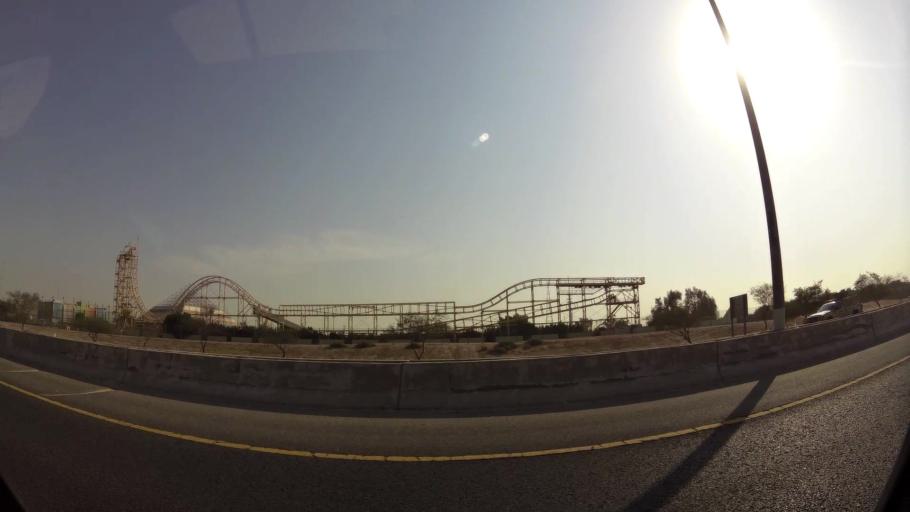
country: KW
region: Al Ahmadi
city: Al Ahmadi
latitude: 29.0881
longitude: 48.0988
